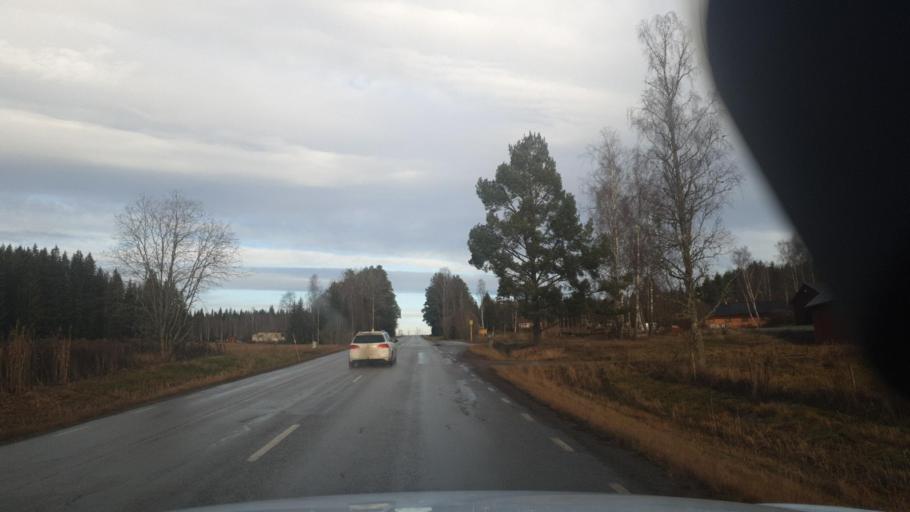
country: SE
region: Vaermland
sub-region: Arvika Kommun
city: Arvika
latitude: 59.6863
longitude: 12.6323
